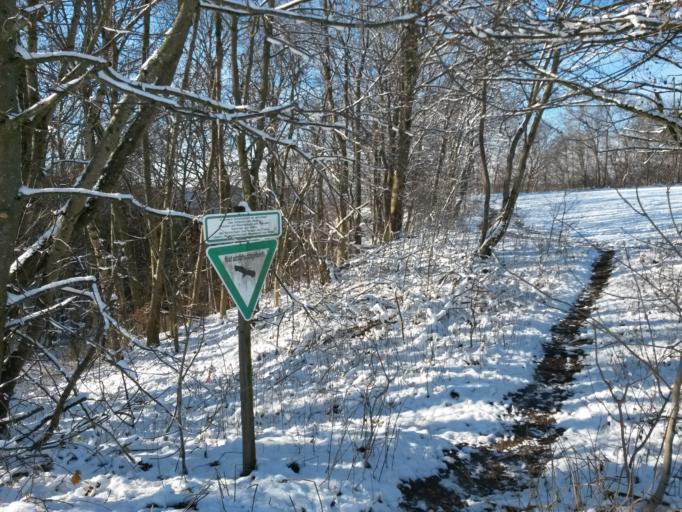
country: DE
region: Baden-Wuerttemberg
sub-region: Regierungsbezirk Stuttgart
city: Bad Uberkingen
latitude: 48.6138
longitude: 9.7730
